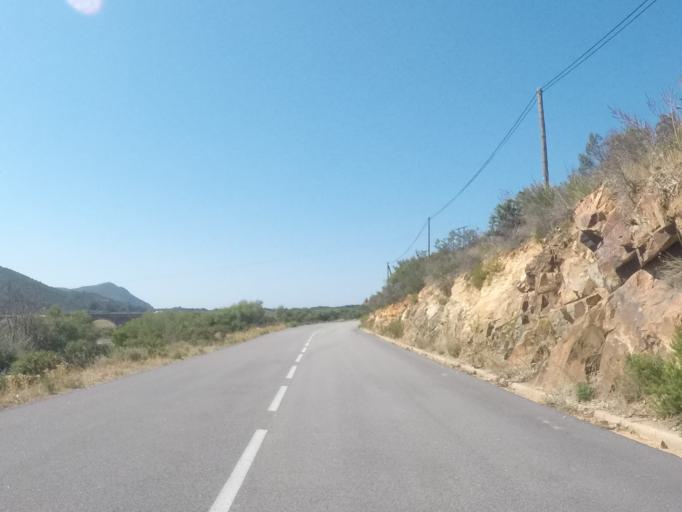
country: FR
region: Corsica
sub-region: Departement de la Haute-Corse
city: Calvi
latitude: 42.4151
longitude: 8.6853
